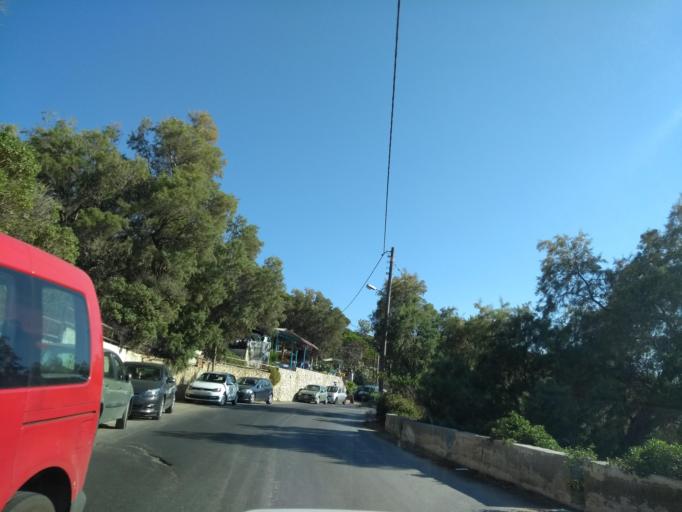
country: GR
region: Crete
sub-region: Nomos Chanias
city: Pithari
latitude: 35.5531
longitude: 24.0864
